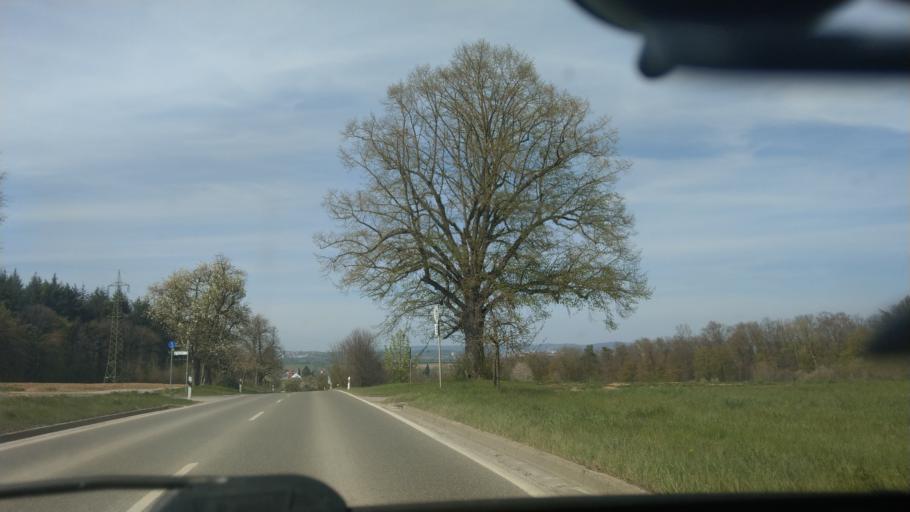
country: DE
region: Baden-Wuerttemberg
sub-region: Regierungsbezirk Stuttgart
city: Wolfschlugen
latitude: 48.6658
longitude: 9.2849
